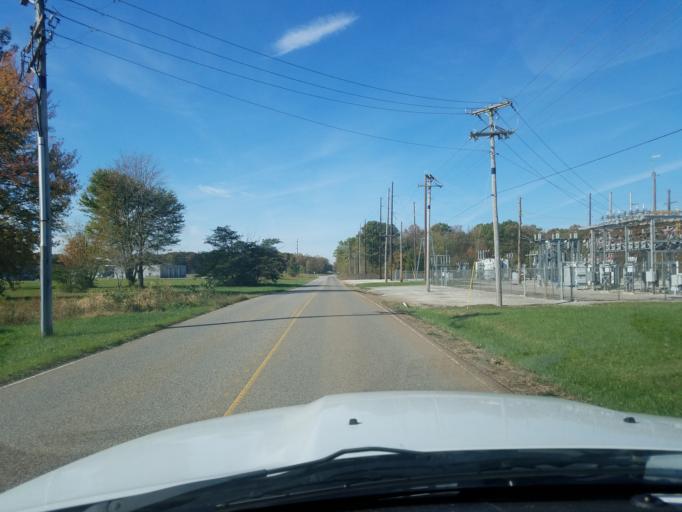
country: US
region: Indiana
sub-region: Jennings County
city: North Vernon
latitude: 39.0365
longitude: -85.6228
